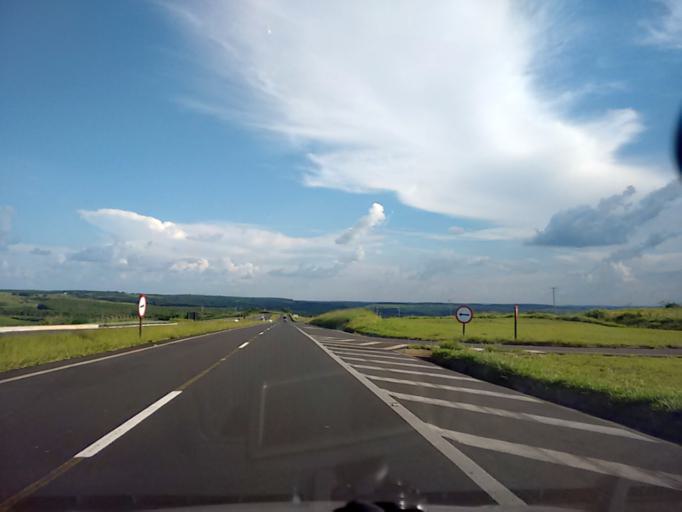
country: BR
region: Sao Paulo
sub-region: Duartina
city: Duartina
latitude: -22.3119
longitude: -49.4943
